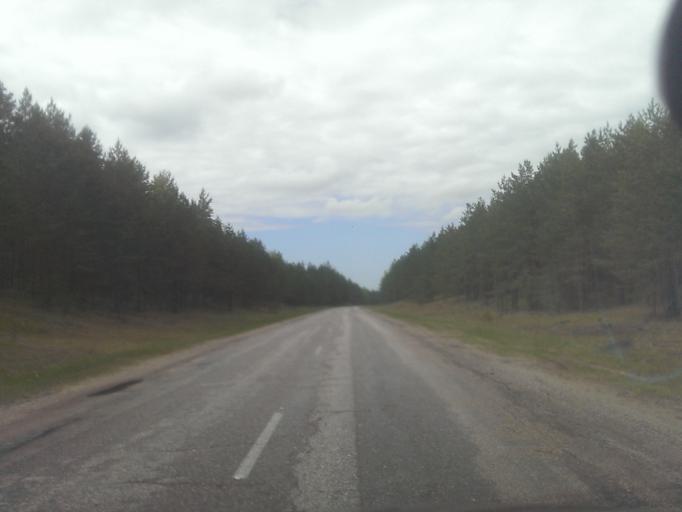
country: LV
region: Ventspils Rajons
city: Piltene
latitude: 57.1152
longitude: 21.7543
